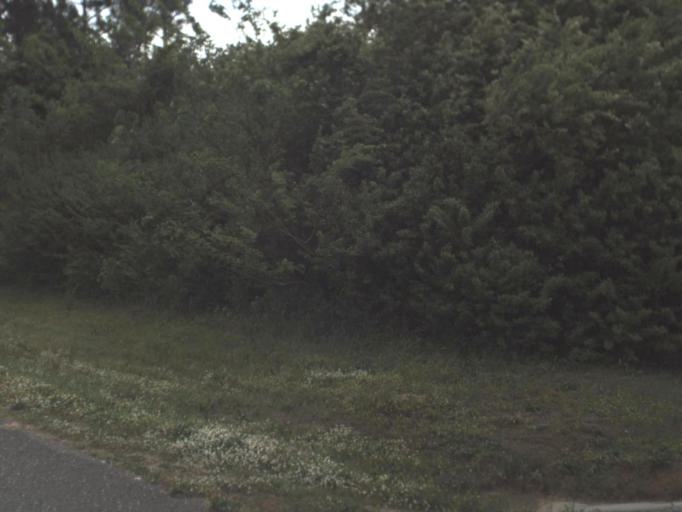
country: US
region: Florida
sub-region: Escambia County
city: Century
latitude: 30.9678
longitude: -87.1369
